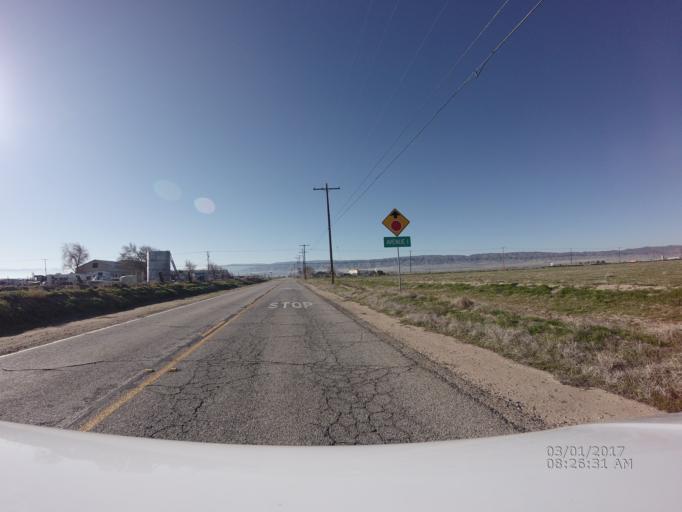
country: US
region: California
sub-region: Los Angeles County
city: Quartz Hill
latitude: 34.7051
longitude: -118.2544
